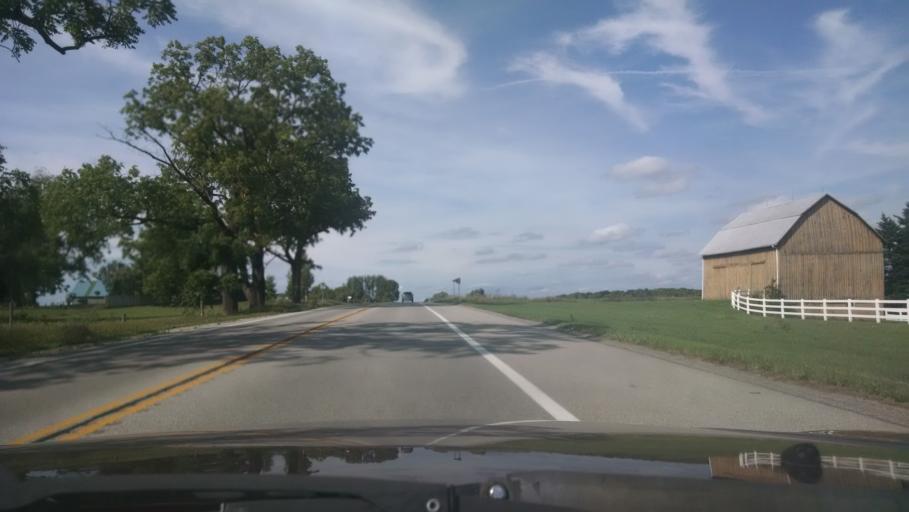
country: US
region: Michigan
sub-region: Grand Traverse County
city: Kingsley
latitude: 44.5635
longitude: -85.6559
